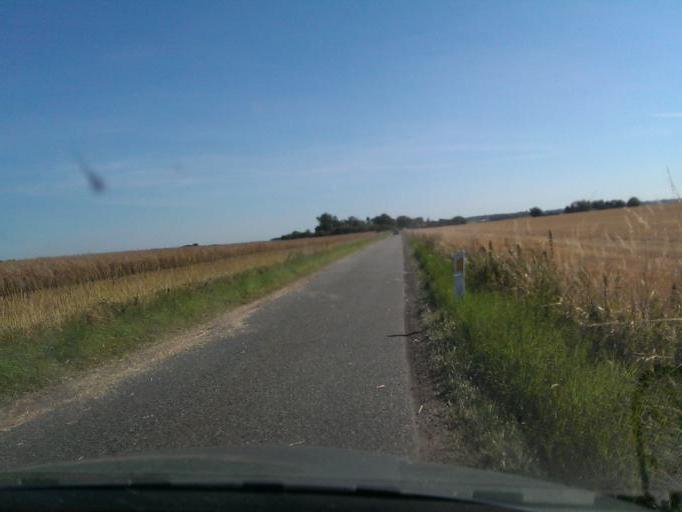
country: DK
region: Central Jutland
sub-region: Hedensted Kommune
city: Juelsminde
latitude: 55.8534
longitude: 10.0474
